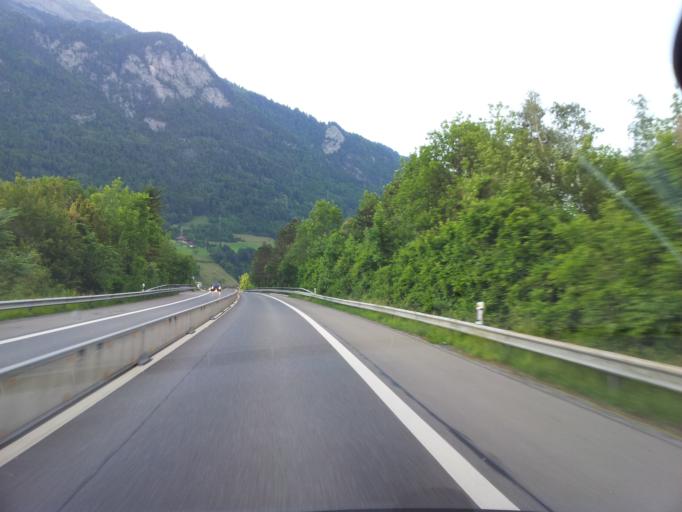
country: CH
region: Obwalden
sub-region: Obwalden
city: Alpnach
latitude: 46.9429
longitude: 8.2780
